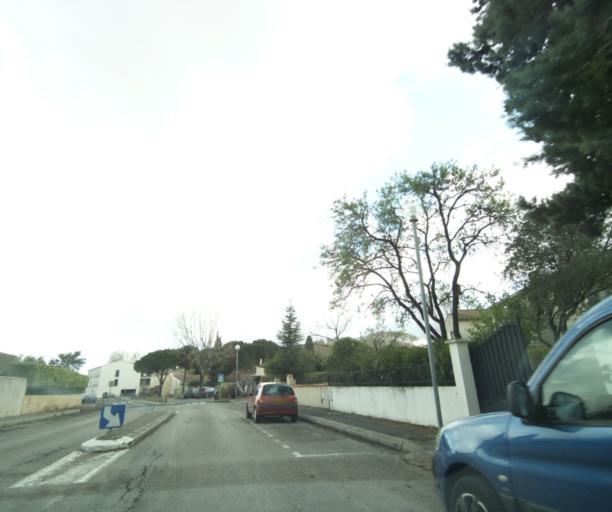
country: FR
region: Languedoc-Roussillon
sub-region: Departement de l'Herault
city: Laverune
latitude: 43.5867
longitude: 3.8029
